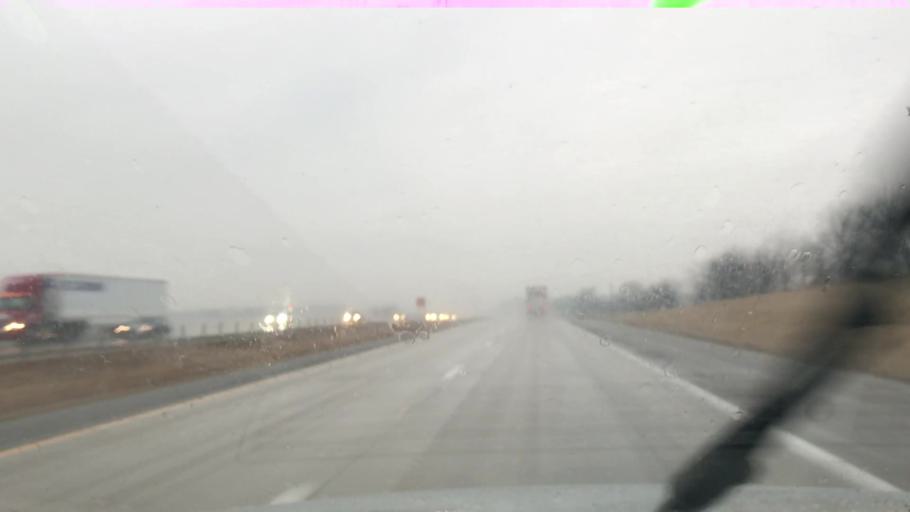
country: US
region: Kentucky
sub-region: Christian County
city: Oak Grove
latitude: 36.6894
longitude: -87.4204
